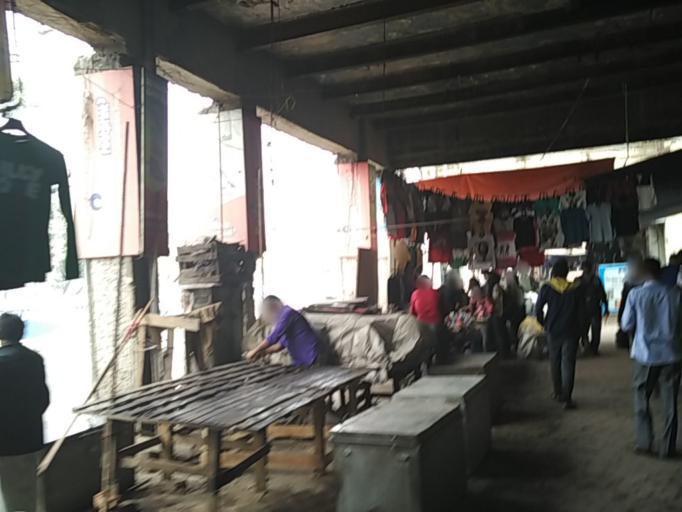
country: IN
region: West Bengal
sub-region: Kolkata
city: Bara Bazar
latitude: 22.5589
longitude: 88.3507
